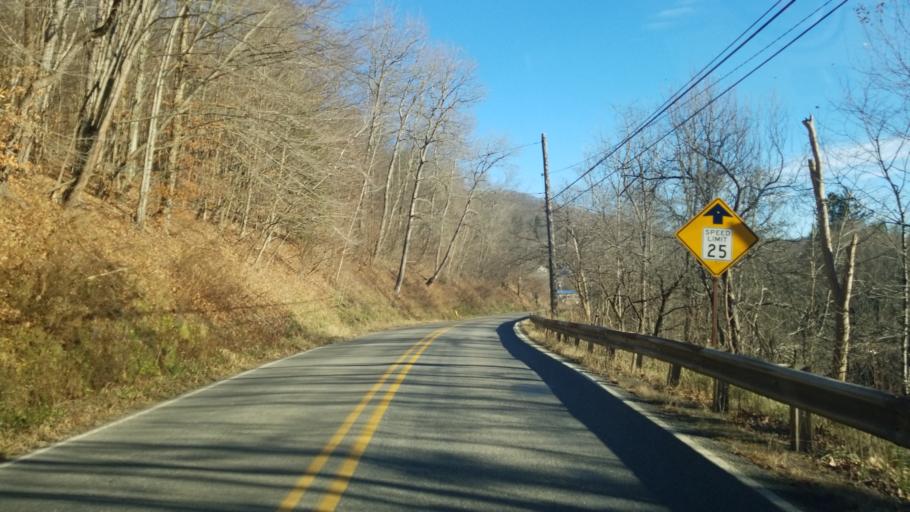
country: US
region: Pennsylvania
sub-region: Potter County
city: Coudersport
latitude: 41.6321
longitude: -78.0963
